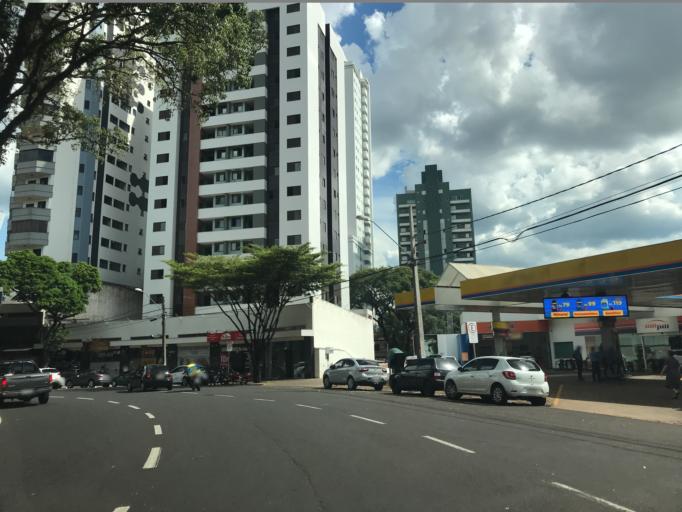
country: BR
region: Parana
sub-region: Maringa
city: Maringa
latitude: -23.4211
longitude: -51.9289
